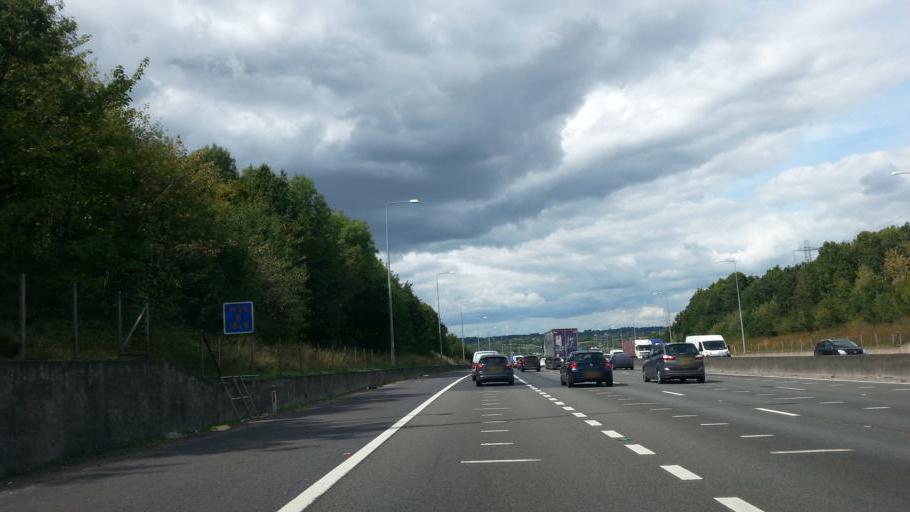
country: GB
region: England
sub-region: Essex
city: Epping
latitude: 51.6700
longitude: 0.1496
